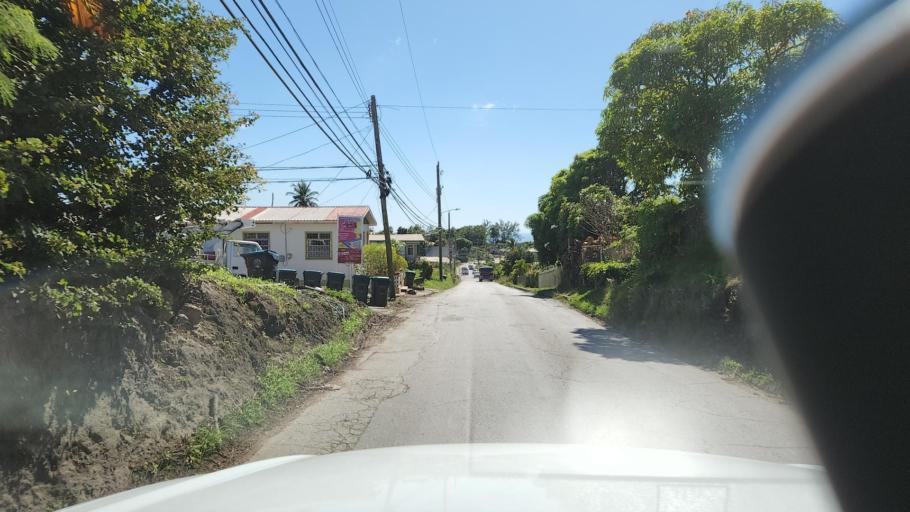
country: BB
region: Saint Thomas
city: Welchman Hall
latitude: 13.1656
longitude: -59.6004
